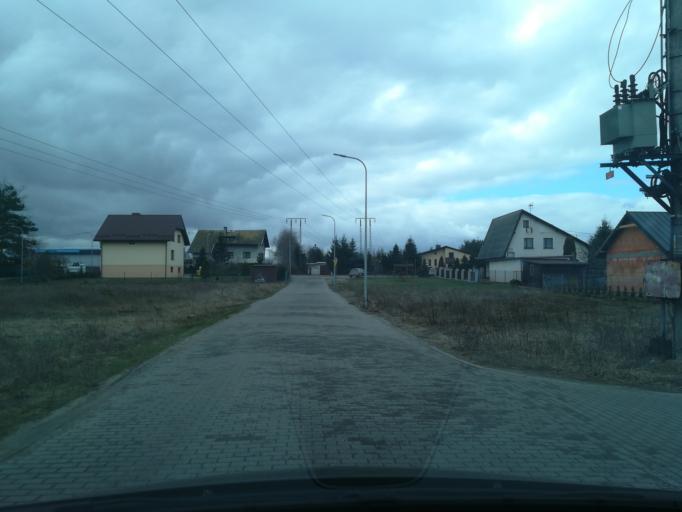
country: PL
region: Kujawsko-Pomorskie
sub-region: Powiat aleksandrowski
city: Ciechocinek
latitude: 52.8739
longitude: 18.7580
